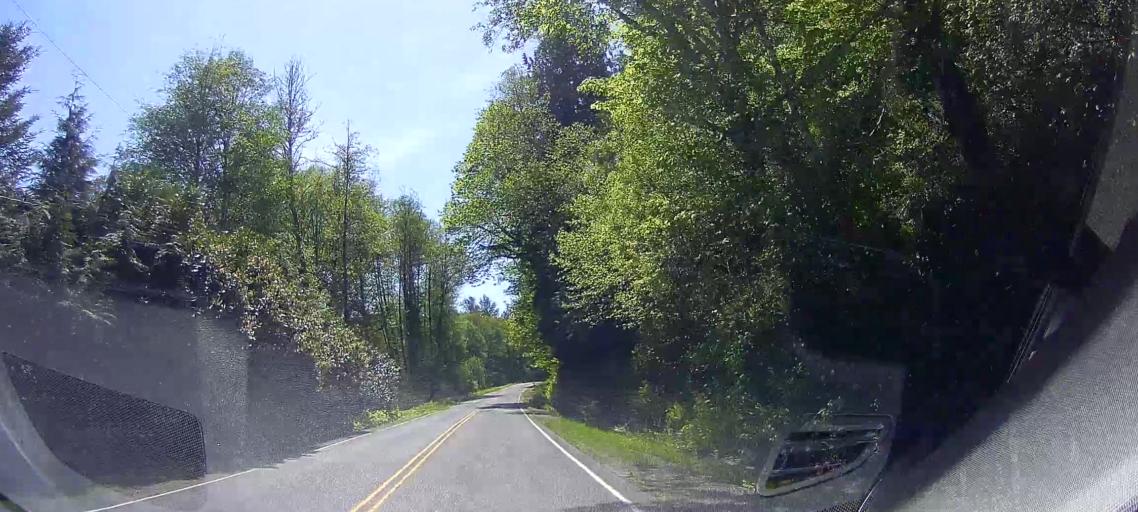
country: US
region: Washington
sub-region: Snohomish County
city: Darrington
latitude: 48.5035
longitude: -121.6633
